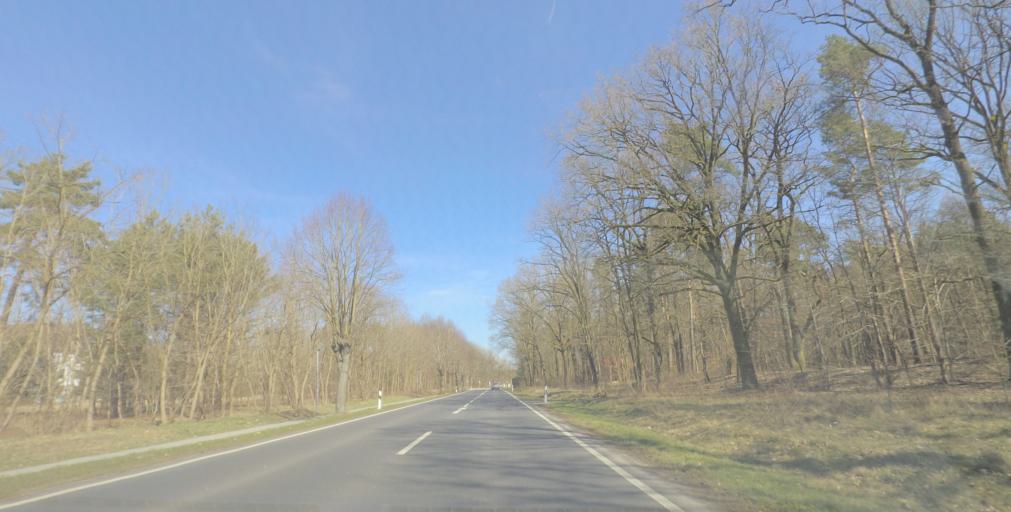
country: DE
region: Brandenburg
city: Neuruppin
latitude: 52.9502
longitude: 12.8317
